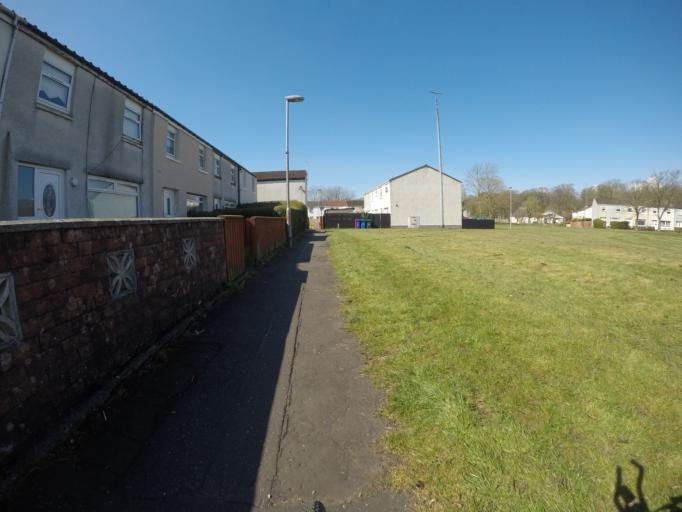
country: GB
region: Scotland
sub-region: North Ayrshire
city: Irvine
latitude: 55.6325
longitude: -4.6646
